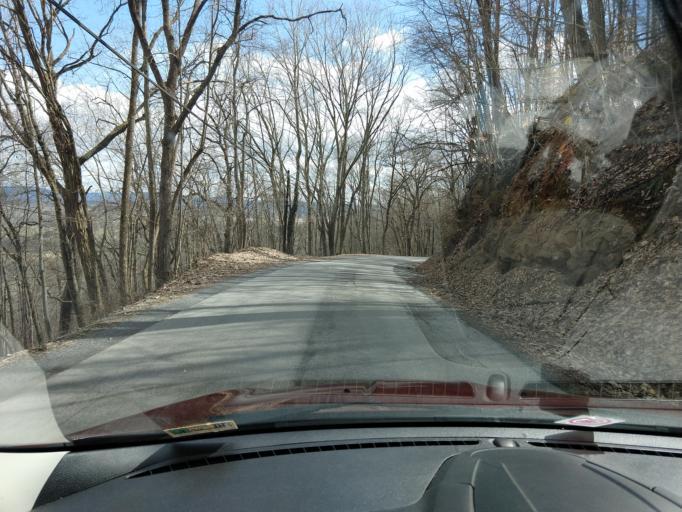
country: US
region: West Virginia
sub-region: Greenbrier County
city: Lewisburg
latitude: 37.8245
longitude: -80.5125
